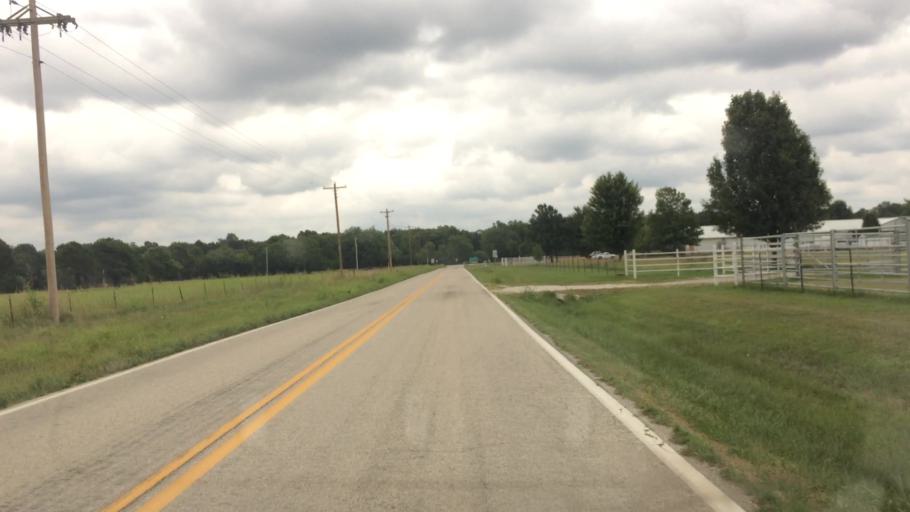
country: US
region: Missouri
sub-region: Greene County
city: Strafford
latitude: 37.2960
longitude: -93.1170
